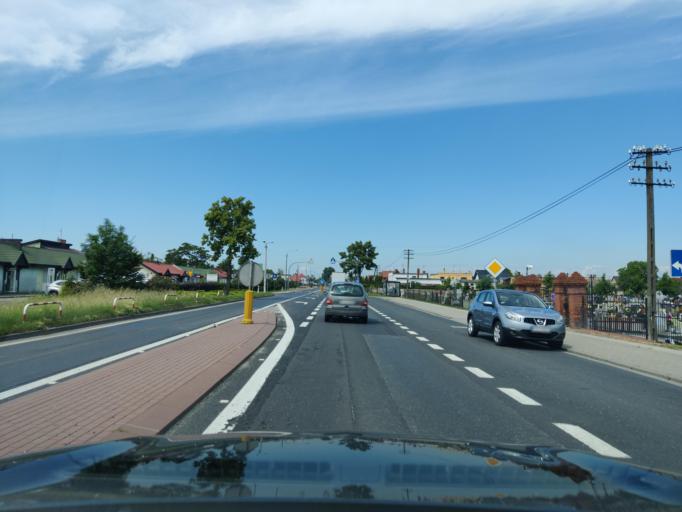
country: PL
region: Greater Poland Voivodeship
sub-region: Powiat grodziski
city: Granowo
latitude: 52.2222
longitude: 16.5387
